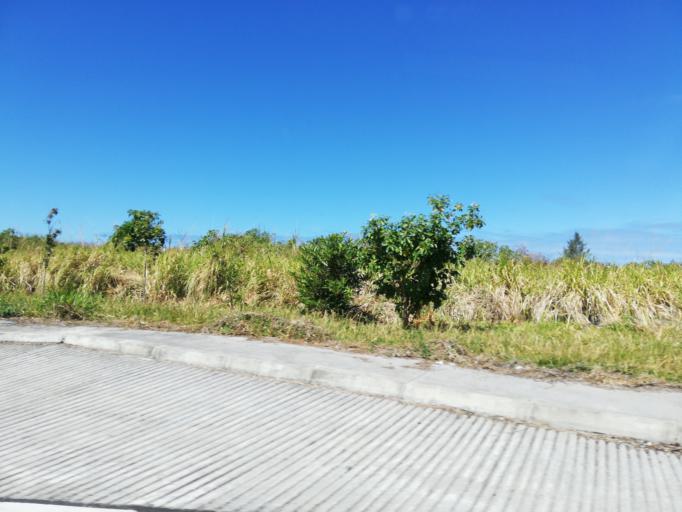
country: MU
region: Grand Port
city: Beau Vallon
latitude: -20.4489
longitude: 57.6967
